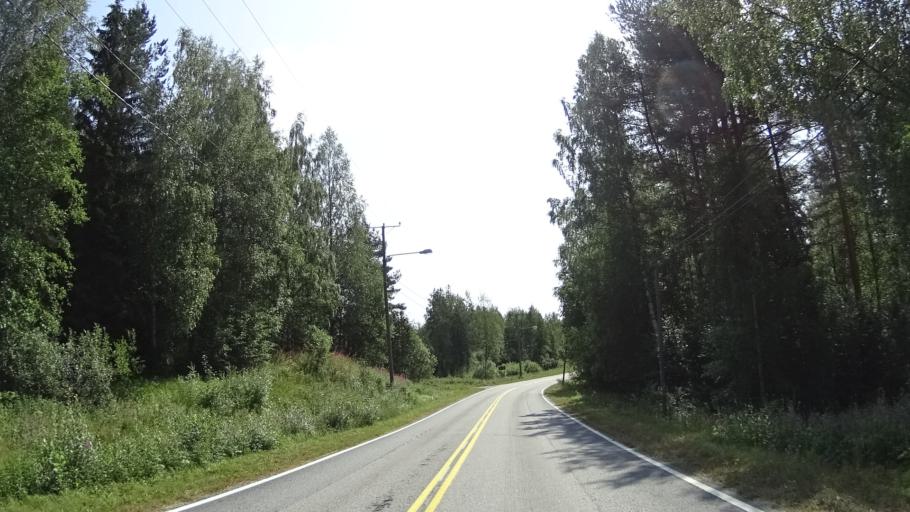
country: FI
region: Pirkanmaa
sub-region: Ylae-Pirkanmaa
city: Maenttae
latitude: 61.8993
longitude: 24.7931
